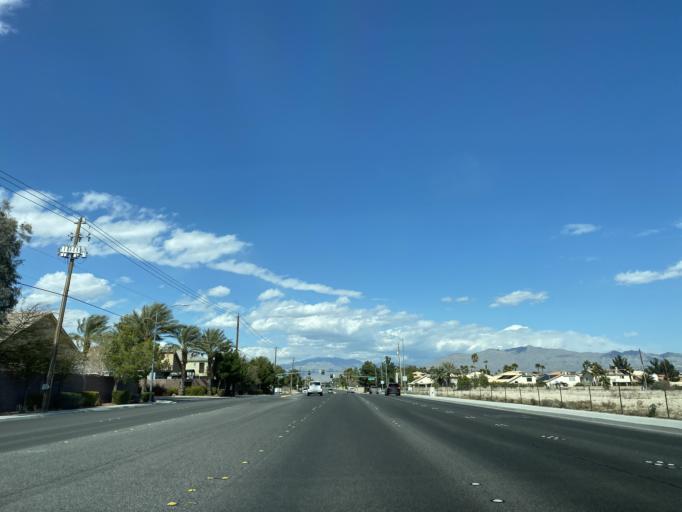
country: US
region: Nevada
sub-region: Clark County
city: Spring Valley
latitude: 36.2388
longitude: -115.2604
